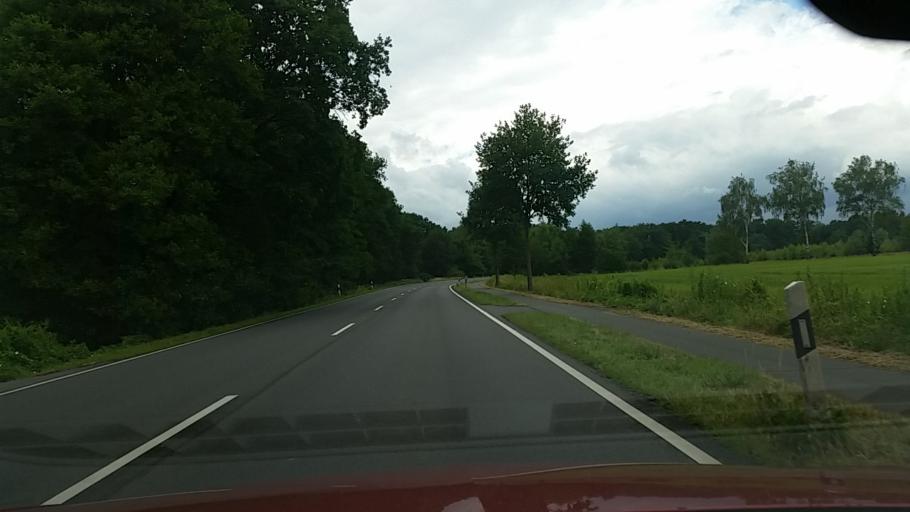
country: DE
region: Lower Saxony
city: Sassenburg
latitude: 52.4963
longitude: 10.6001
